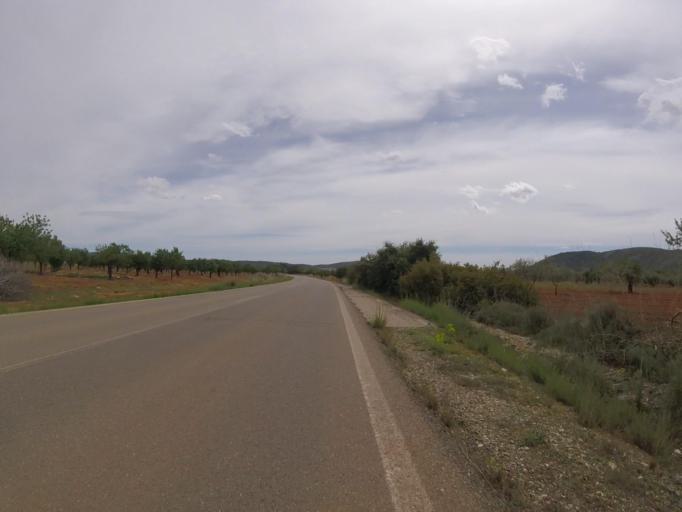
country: ES
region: Valencia
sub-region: Provincia de Castello
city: Cabanes
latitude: 40.1661
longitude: 0.0090
